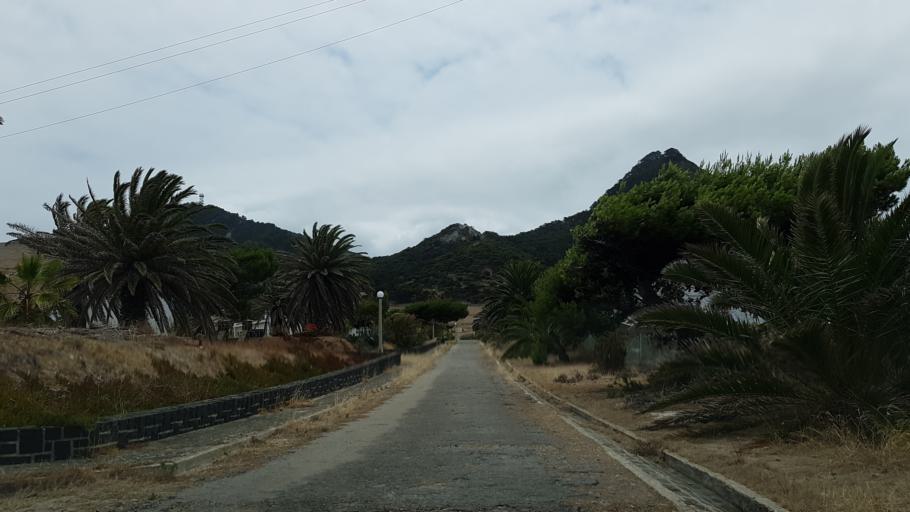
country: PT
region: Madeira
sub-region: Porto Santo
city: Camacha
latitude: 33.0877
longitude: -16.3407
